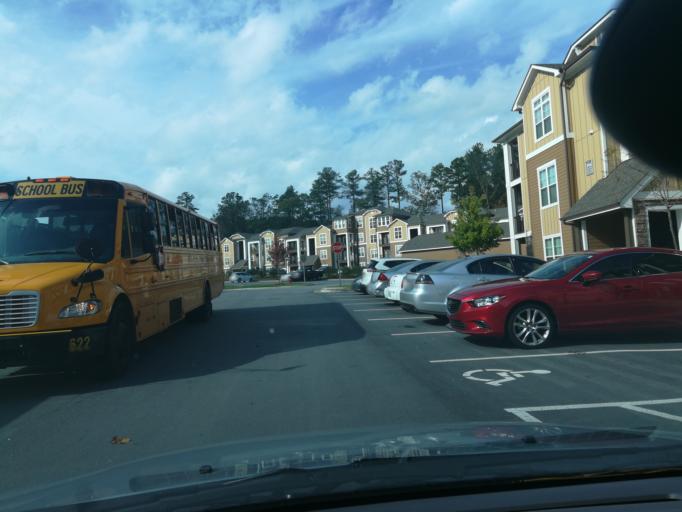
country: US
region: North Carolina
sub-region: Durham County
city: Durham
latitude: 36.0588
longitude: -78.9411
